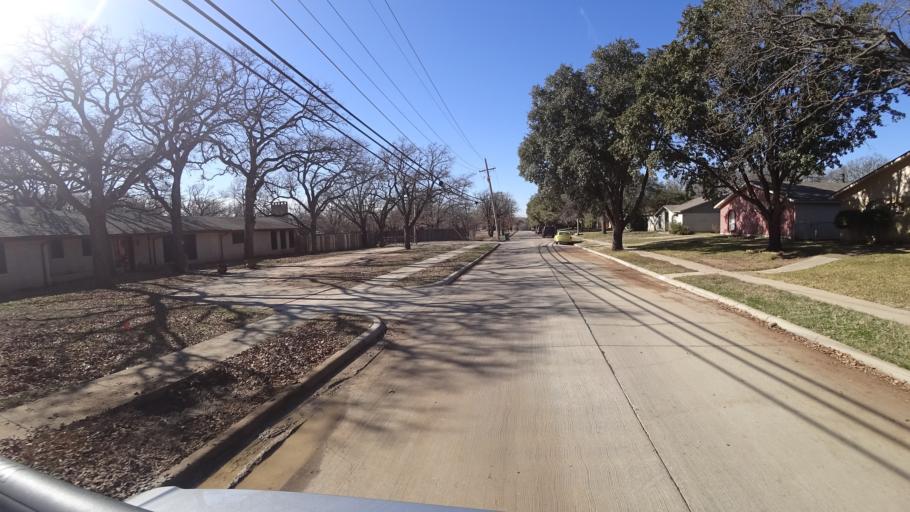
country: US
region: Texas
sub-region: Denton County
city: Lewisville
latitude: 33.0314
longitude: -97.0254
